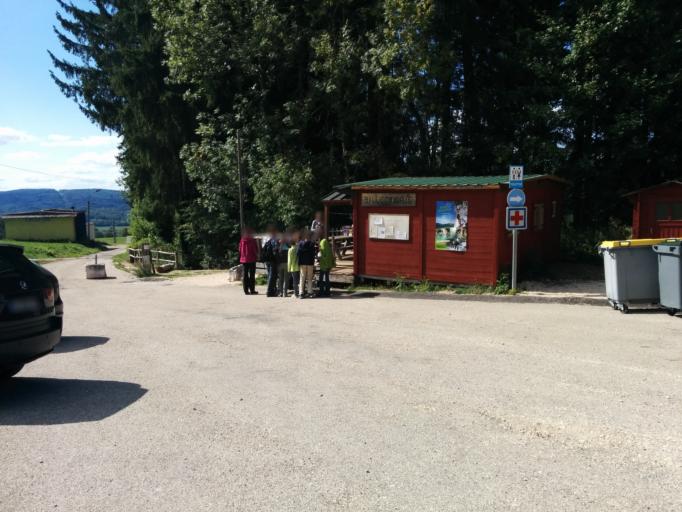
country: FR
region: Rhone-Alpes
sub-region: Departement de l'Ain
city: Hauteville-Lompnes
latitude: 45.9879
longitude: 5.6189
